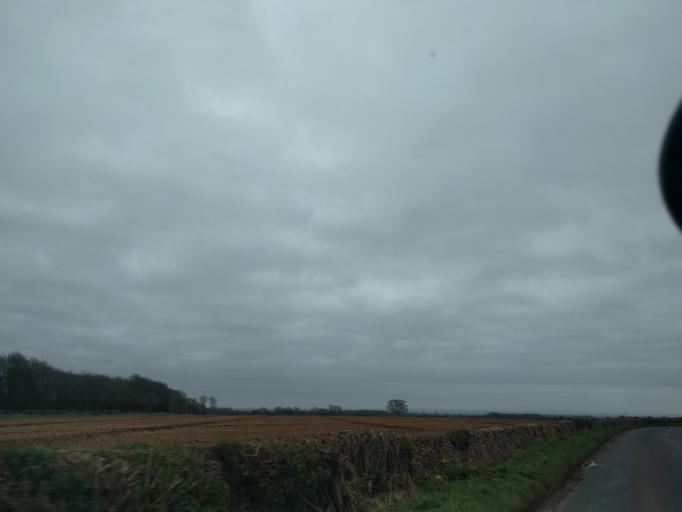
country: GB
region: England
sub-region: Gloucestershire
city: Nailsworth
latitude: 51.6564
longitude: -2.2600
